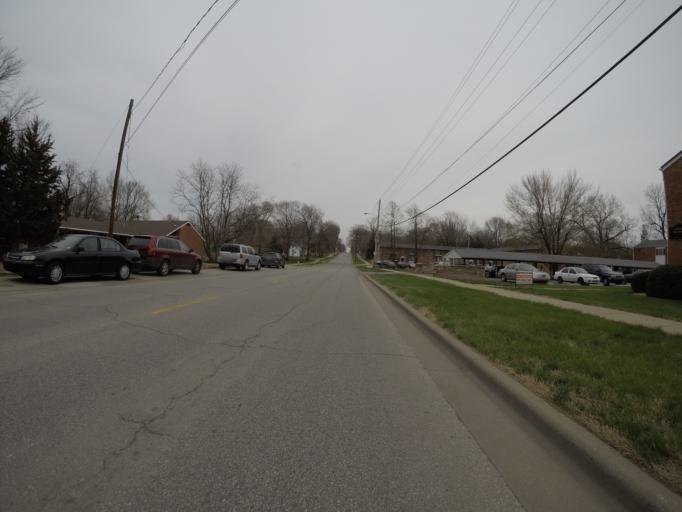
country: US
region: Kansas
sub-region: Johnson County
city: Olathe
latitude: 38.8805
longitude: -94.8152
